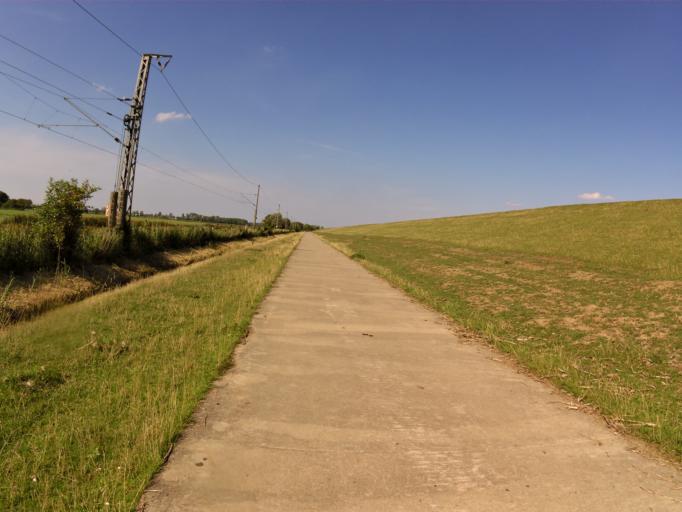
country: DE
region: Lower Saxony
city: Nordenham
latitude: 53.4489
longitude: 8.4756
